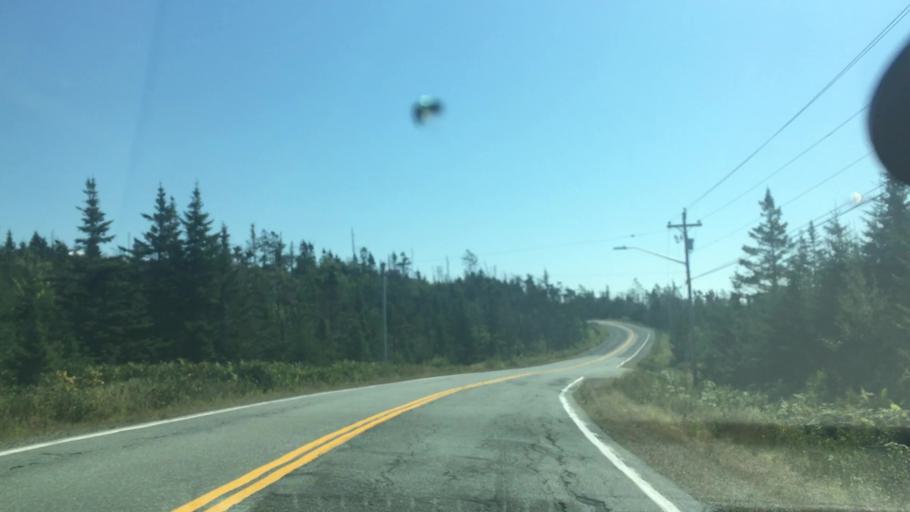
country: CA
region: Nova Scotia
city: New Glasgow
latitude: 44.9170
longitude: -62.3207
